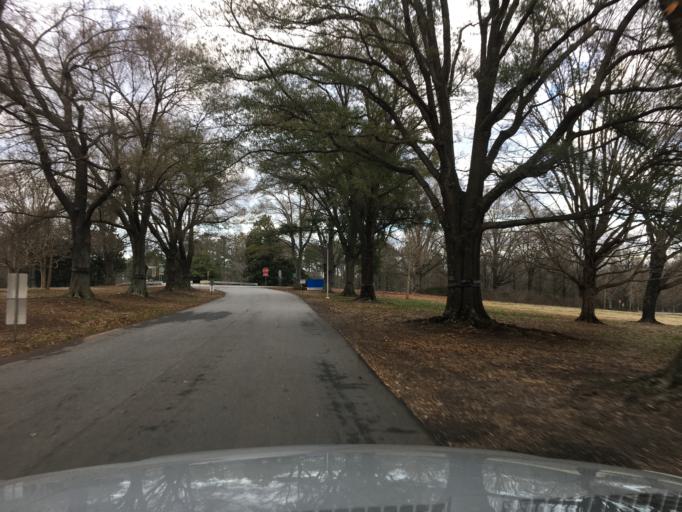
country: US
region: South Carolina
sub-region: Spartanburg County
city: Valley Falls
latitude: 34.9905
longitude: -81.9588
